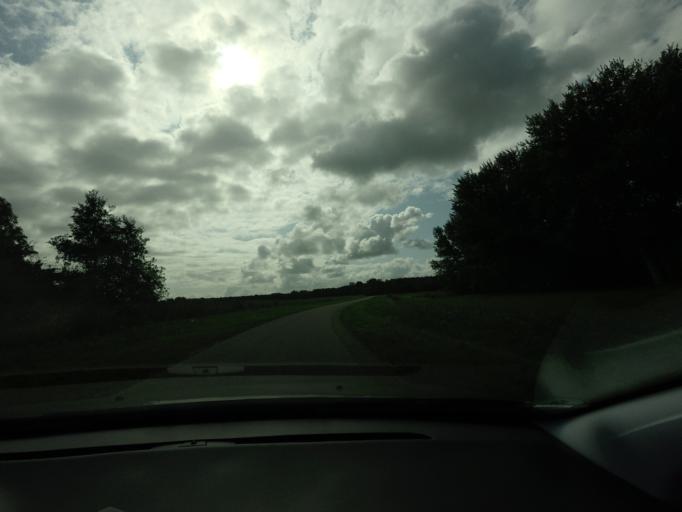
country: NL
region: North Holland
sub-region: Gemeente Hollands Kroon
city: Den Oever
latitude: 52.8927
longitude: 5.0729
